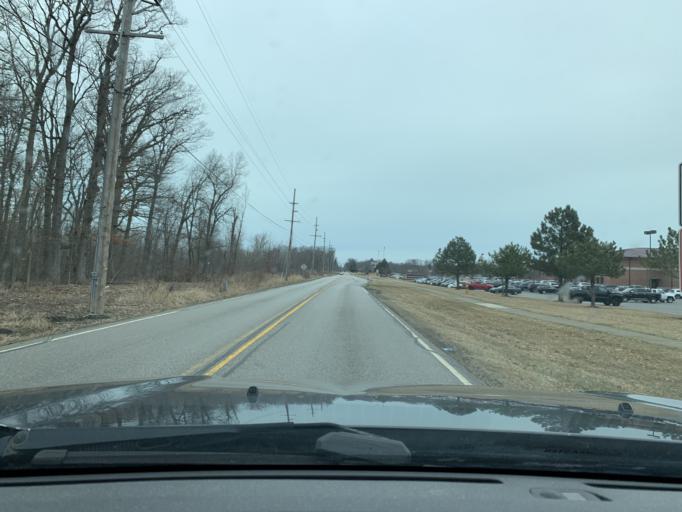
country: US
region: Indiana
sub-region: Porter County
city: Chesterton
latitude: 41.5867
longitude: -87.0667
